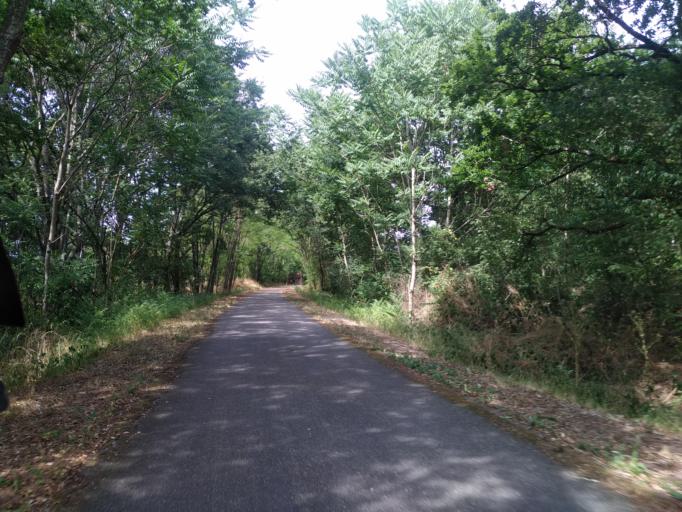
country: FR
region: Auvergne
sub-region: Departement de l'Allier
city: Diou
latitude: 46.5499
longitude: 3.7415
